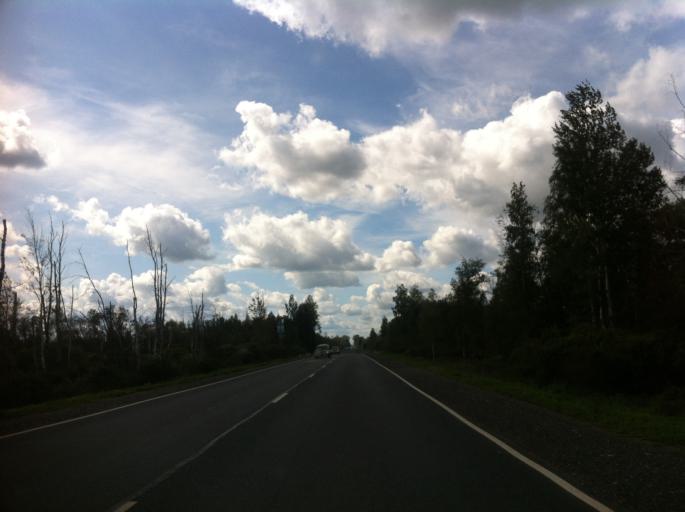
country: RU
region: Pskov
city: Palkino
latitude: 57.7648
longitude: 28.1049
